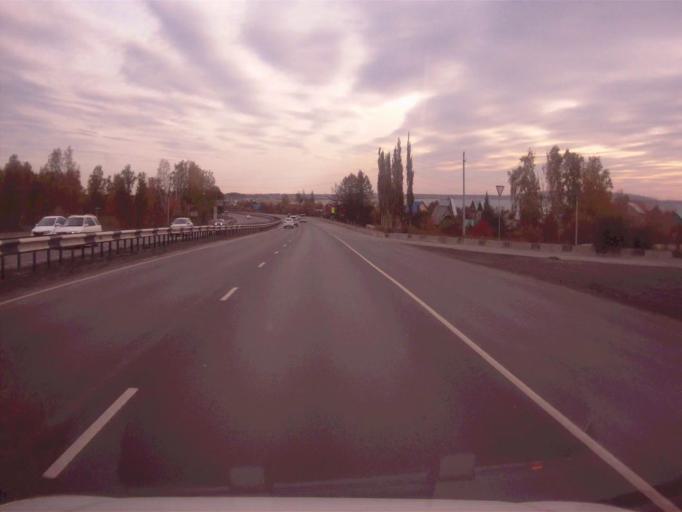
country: RU
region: Chelyabinsk
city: Novosineglazovskiy
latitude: 55.0376
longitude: 61.4414
